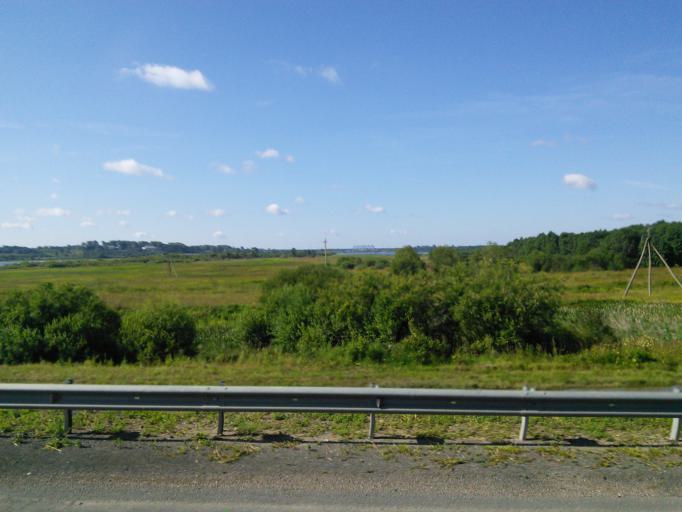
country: RU
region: Vologda
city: Sheksna
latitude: 59.2167
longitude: 38.4884
